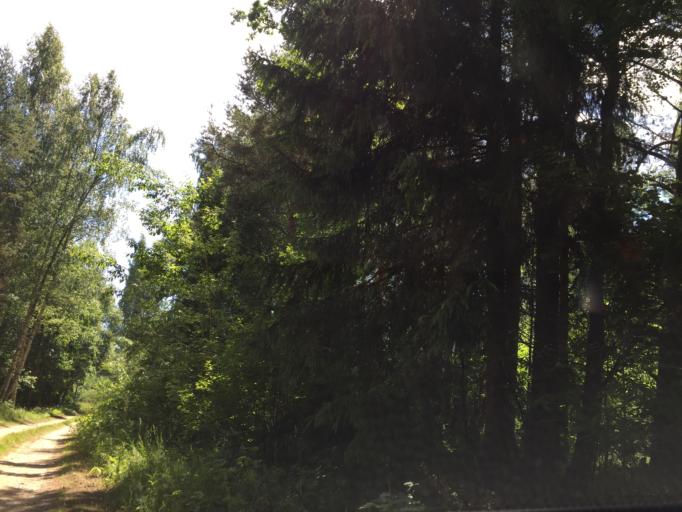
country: LV
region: Kuldigas Rajons
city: Kuldiga
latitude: 57.0996
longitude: 21.8923
